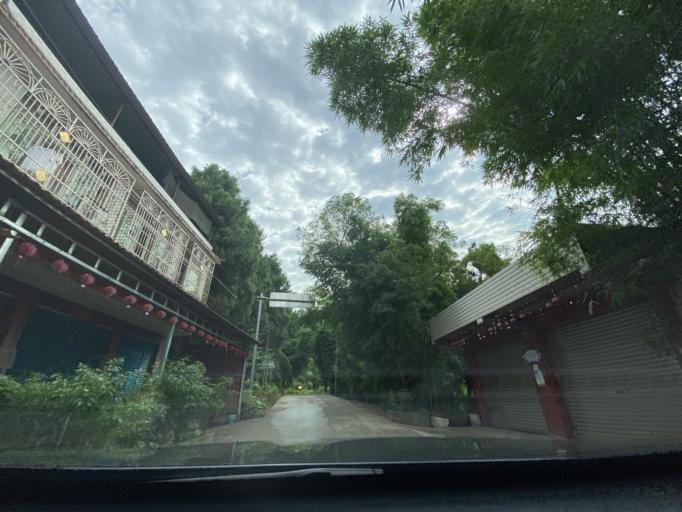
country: CN
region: Sichuan
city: Jiancheng
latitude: 30.4872
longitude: 104.6269
